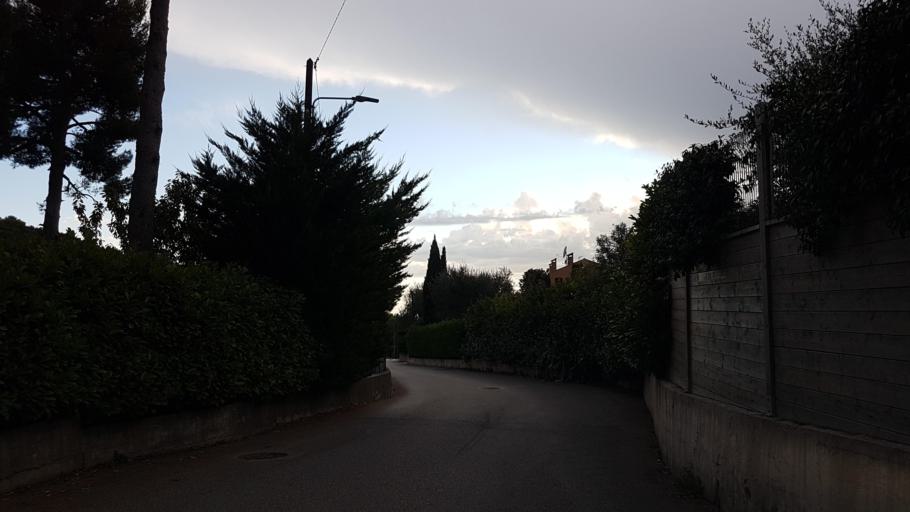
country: FR
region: Provence-Alpes-Cote d'Azur
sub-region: Departement des Alpes-Maritimes
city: La Turbie
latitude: 43.7346
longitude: 7.3935
